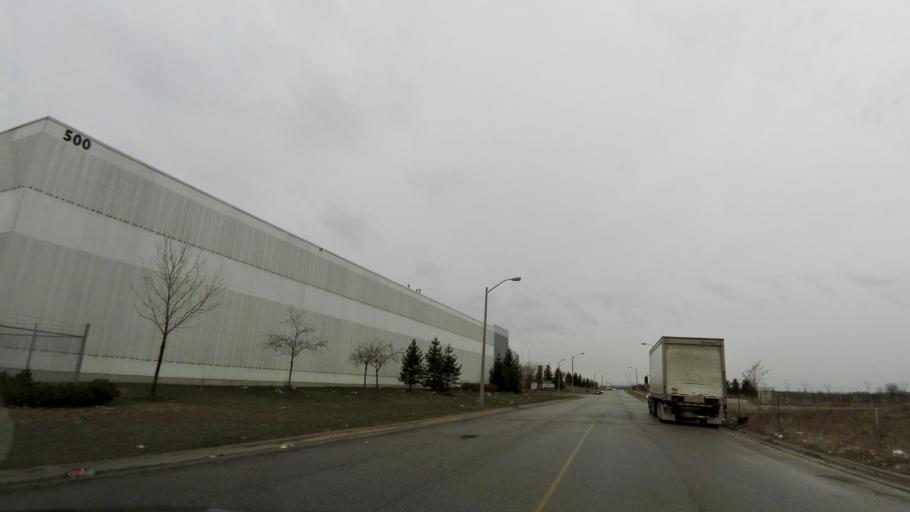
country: CA
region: Ontario
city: Etobicoke
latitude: 43.7770
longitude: -79.6394
